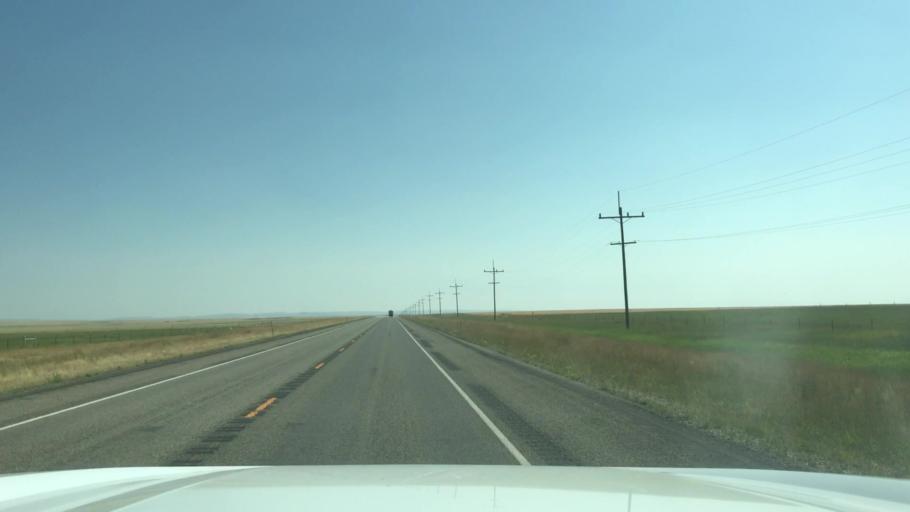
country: US
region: Montana
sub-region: Wheatland County
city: Harlowton
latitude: 46.5141
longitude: -109.7659
